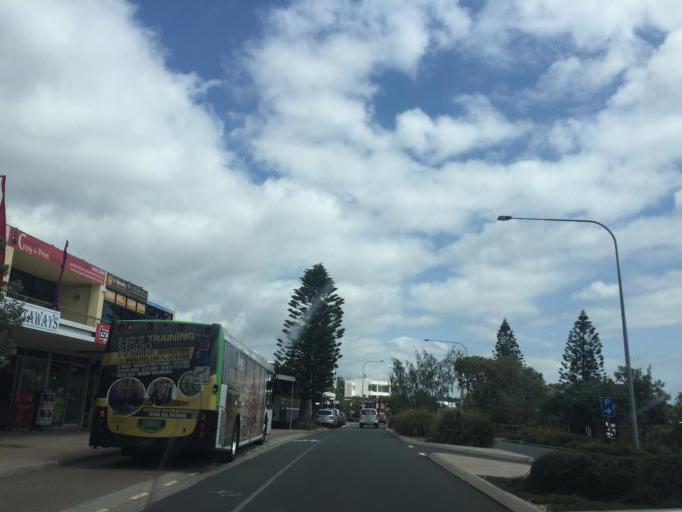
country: AU
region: Queensland
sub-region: Sunshine Coast
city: Coolum Beach
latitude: -26.5302
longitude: 153.0914
